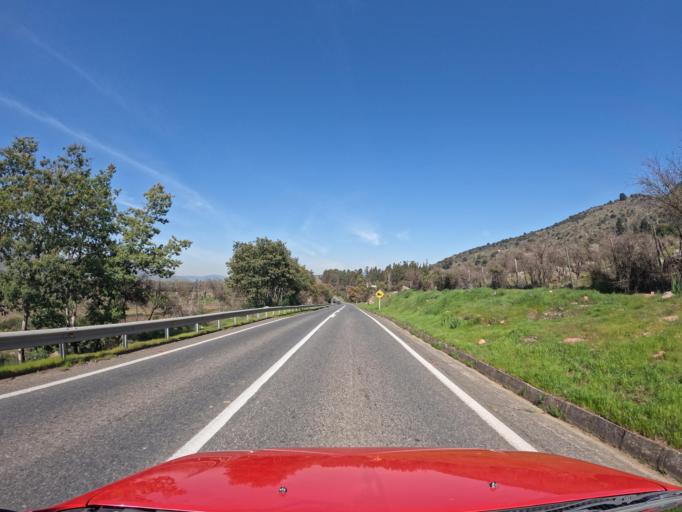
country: CL
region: Maule
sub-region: Provincia de Curico
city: Rauco
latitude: -35.0672
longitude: -71.6240
